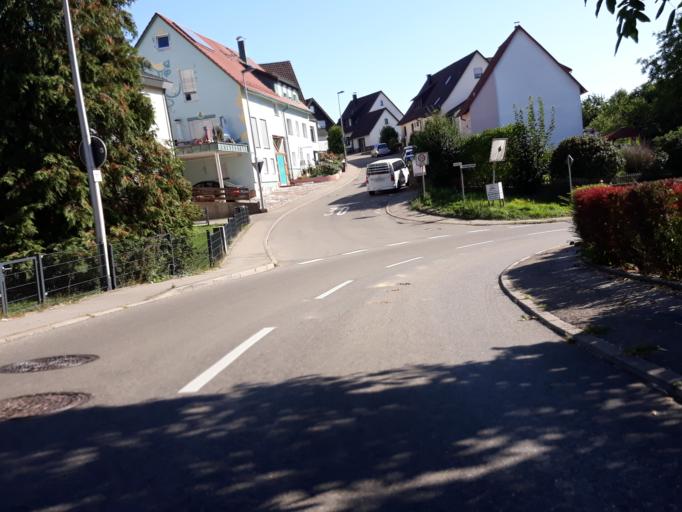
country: DE
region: Baden-Wuerttemberg
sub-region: Regierungsbezirk Stuttgart
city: Aidlingen
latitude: 48.7118
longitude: 8.9158
